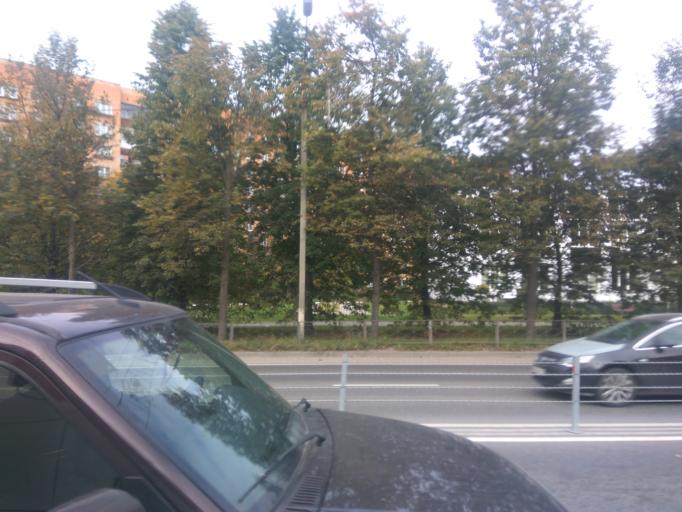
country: RU
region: Moskovskaya
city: Fryazino
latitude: 55.9513
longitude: 38.0506
